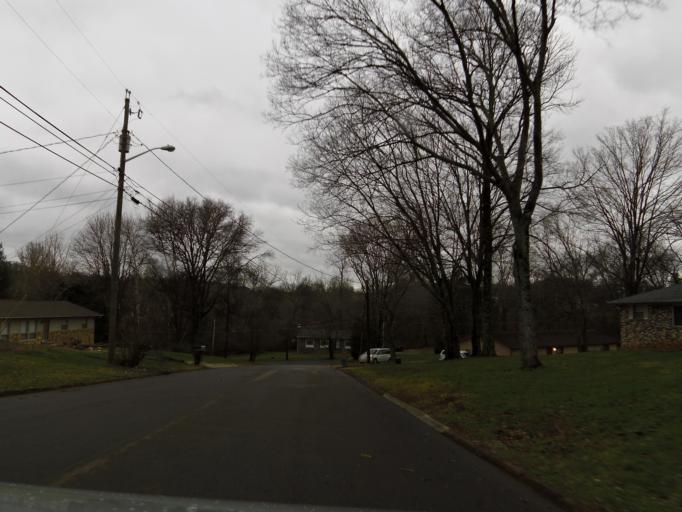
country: US
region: Tennessee
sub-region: Knox County
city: Knoxville
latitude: 35.9775
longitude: -84.0024
